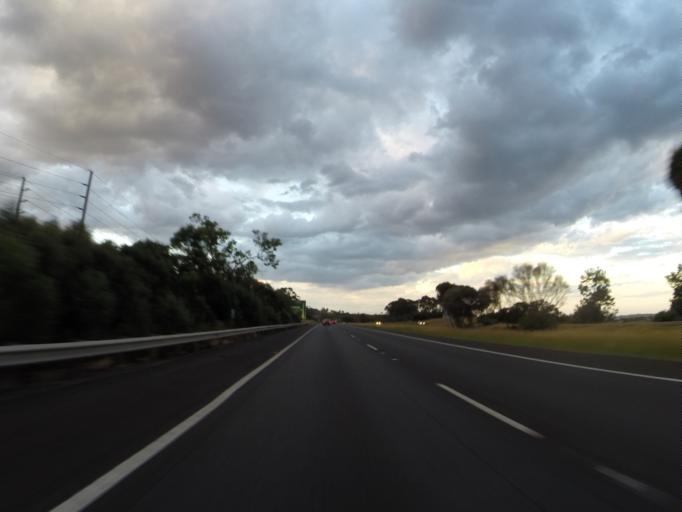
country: AU
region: New South Wales
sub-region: Campbelltown Municipality
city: Glen Alpine
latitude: -34.0727
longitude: 150.7768
